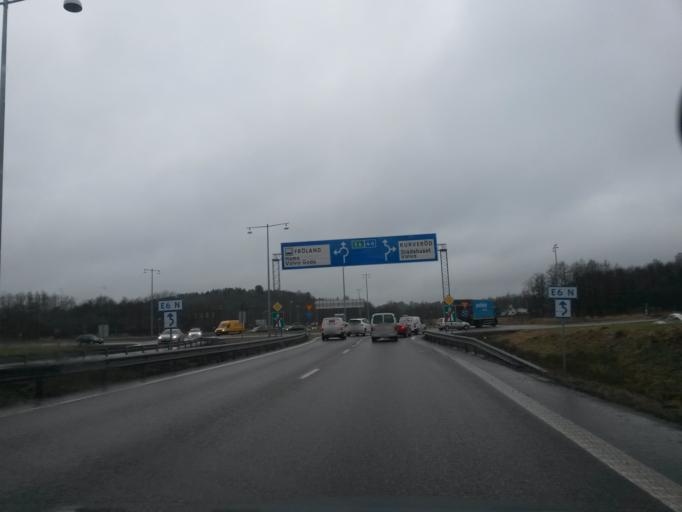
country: SE
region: Vaestra Goetaland
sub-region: Uddevalla Kommun
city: Uddevalla
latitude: 58.3523
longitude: 11.8719
